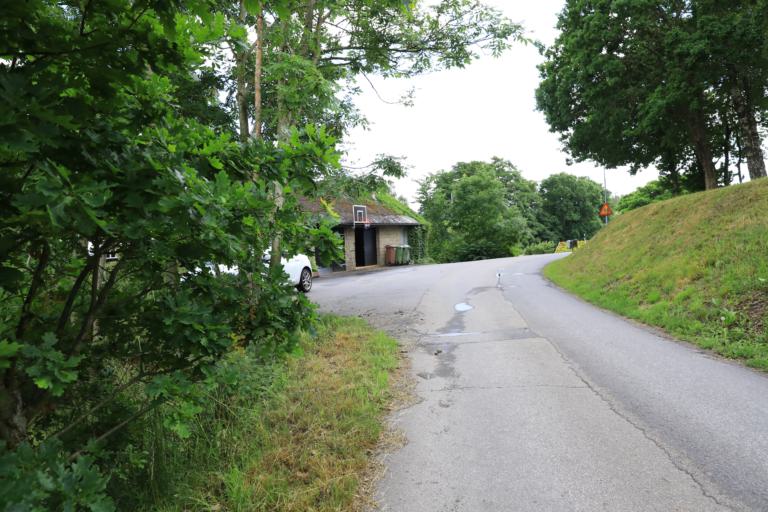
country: SE
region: Halland
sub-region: Varbergs Kommun
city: Varberg
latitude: 57.1774
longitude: 12.2979
